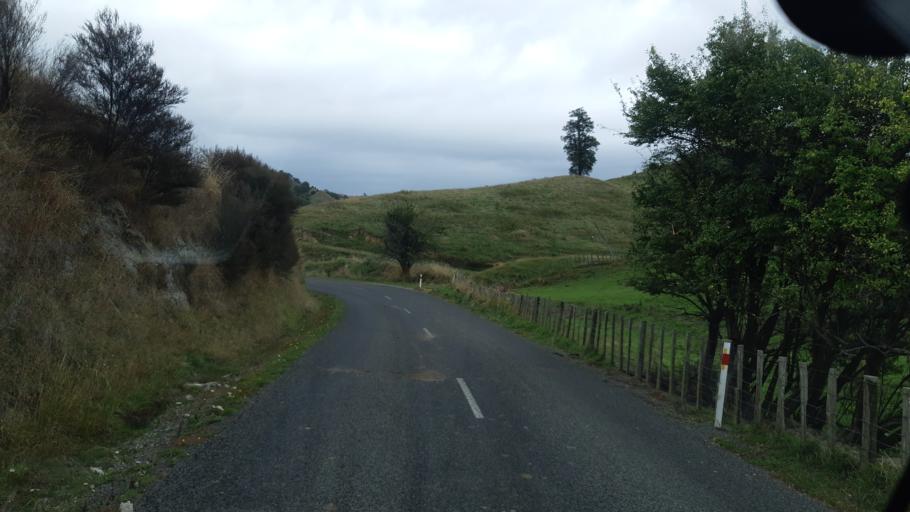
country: NZ
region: Manawatu-Wanganui
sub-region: Ruapehu District
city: Waiouru
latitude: -39.5548
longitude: 175.5873
